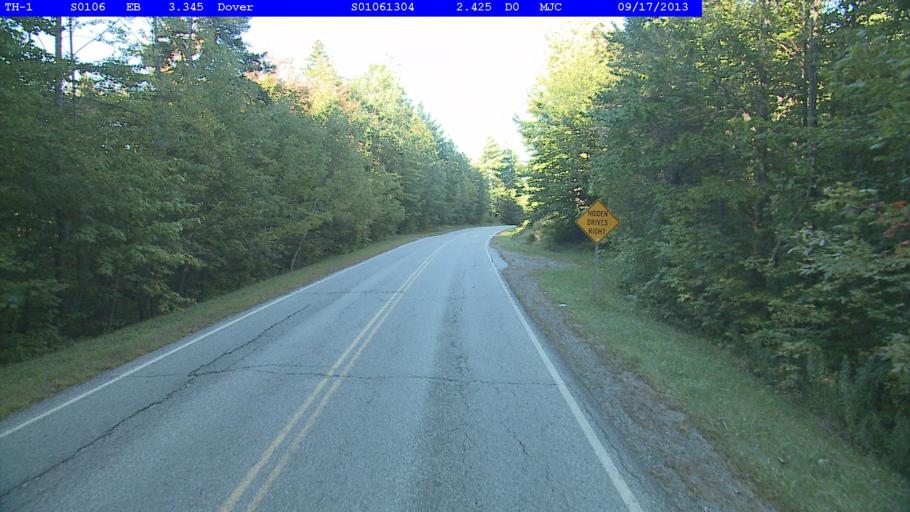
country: US
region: Vermont
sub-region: Windham County
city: Dover
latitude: 42.9451
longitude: -72.7983
